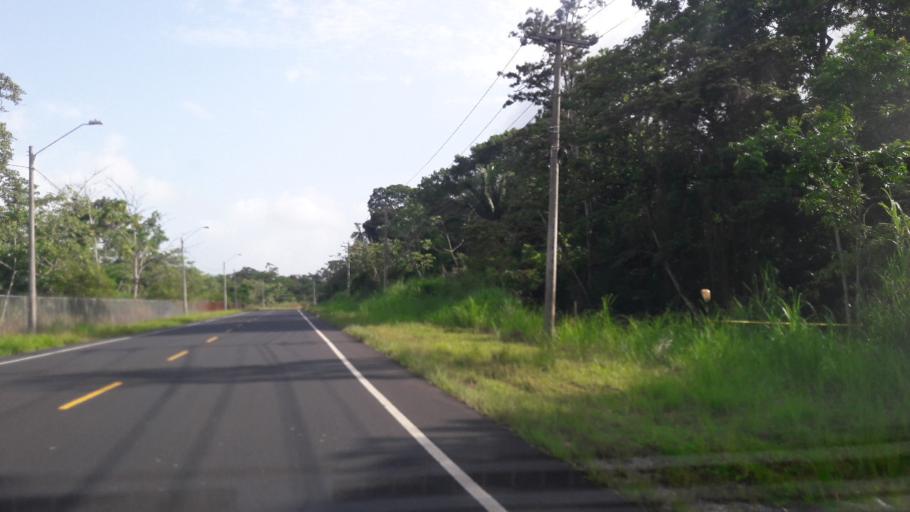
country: PA
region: Colon
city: Cativa
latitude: 9.3547
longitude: -79.8626
